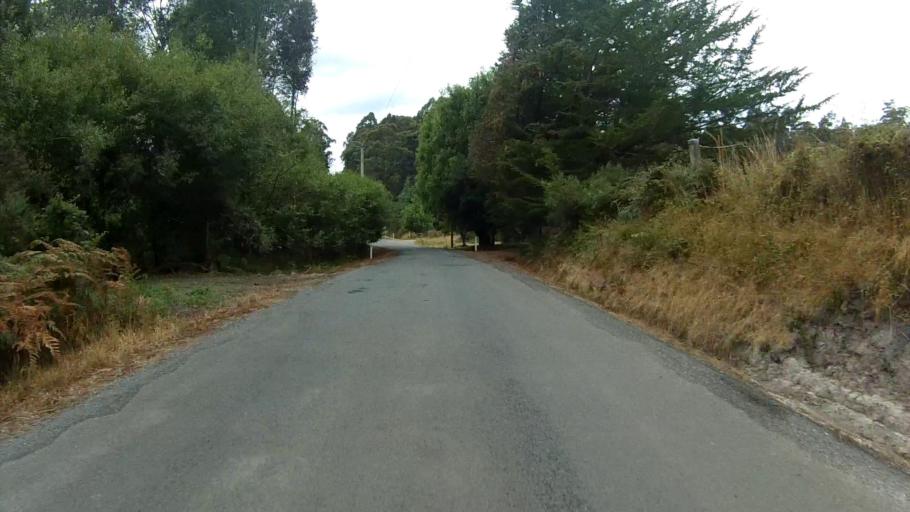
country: AU
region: Tasmania
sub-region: Huon Valley
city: Cygnet
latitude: -43.2338
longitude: 147.1577
